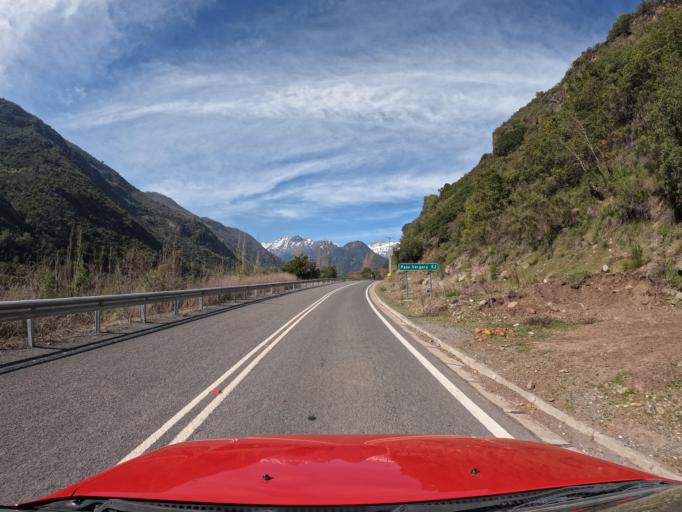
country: CL
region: O'Higgins
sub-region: Provincia de Colchagua
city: Chimbarongo
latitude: -35.0005
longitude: -70.8010
